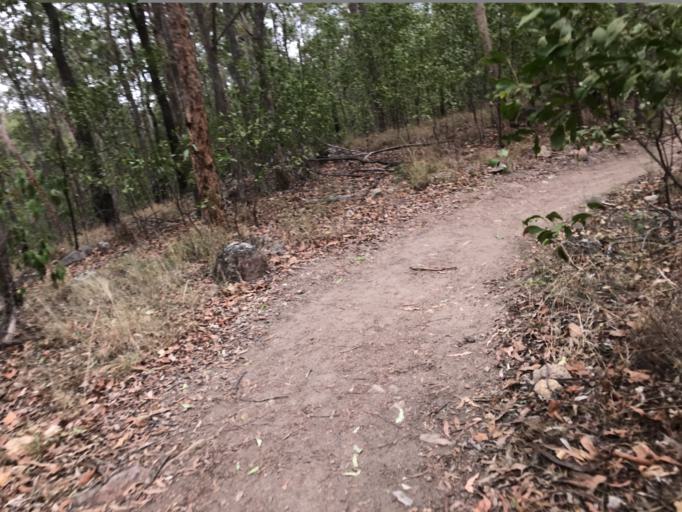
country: AU
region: Queensland
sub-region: Brisbane
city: Taringa
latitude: -27.4681
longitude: 152.9523
